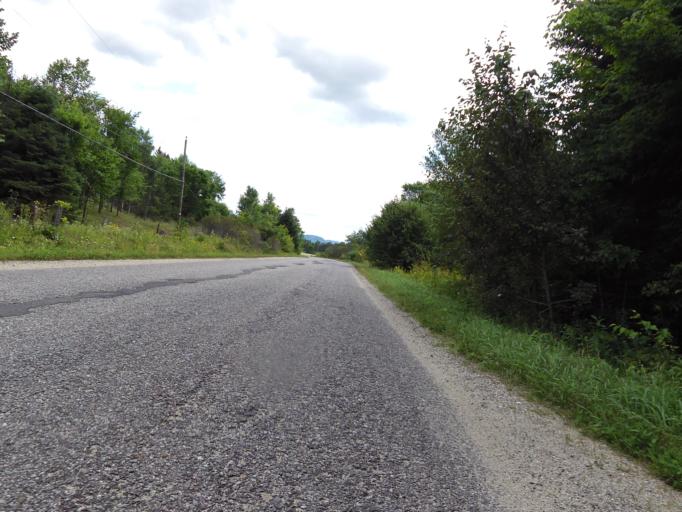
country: CA
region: Quebec
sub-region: Outaouais
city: Wakefield
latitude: 45.8089
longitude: -76.0024
